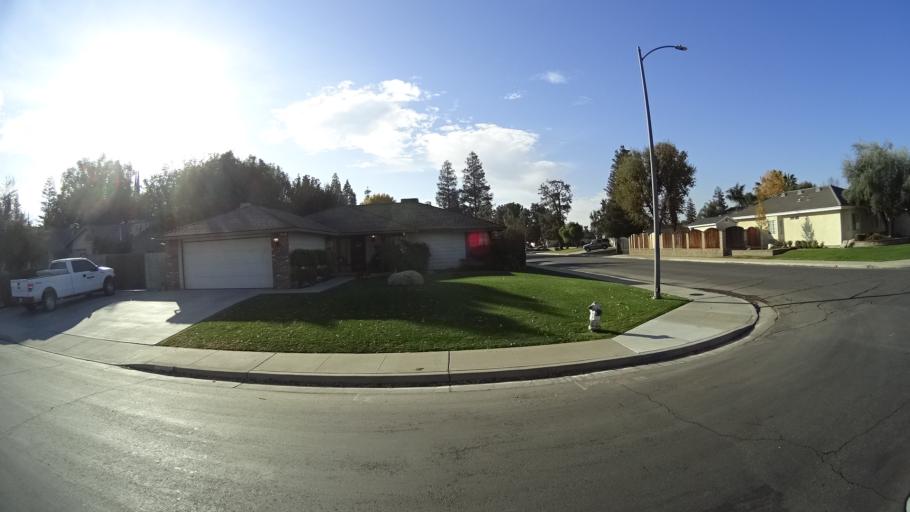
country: US
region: California
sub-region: Kern County
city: Rosedale
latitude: 35.3517
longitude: -119.1526
